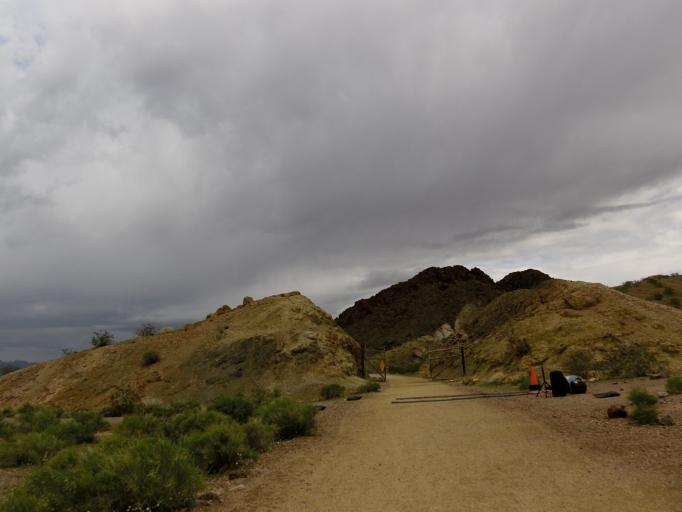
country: US
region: Nevada
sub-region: Clark County
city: Boulder City
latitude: 36.0109
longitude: -114.7913
